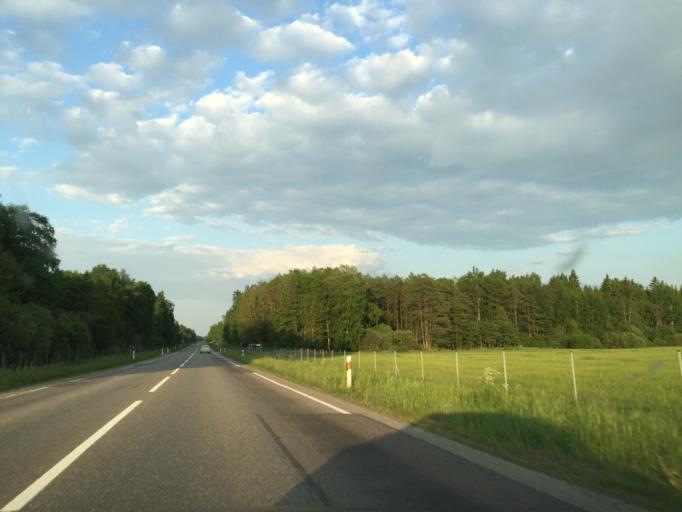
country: LT
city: Kursenai
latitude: 56.0038
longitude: 22.7486
